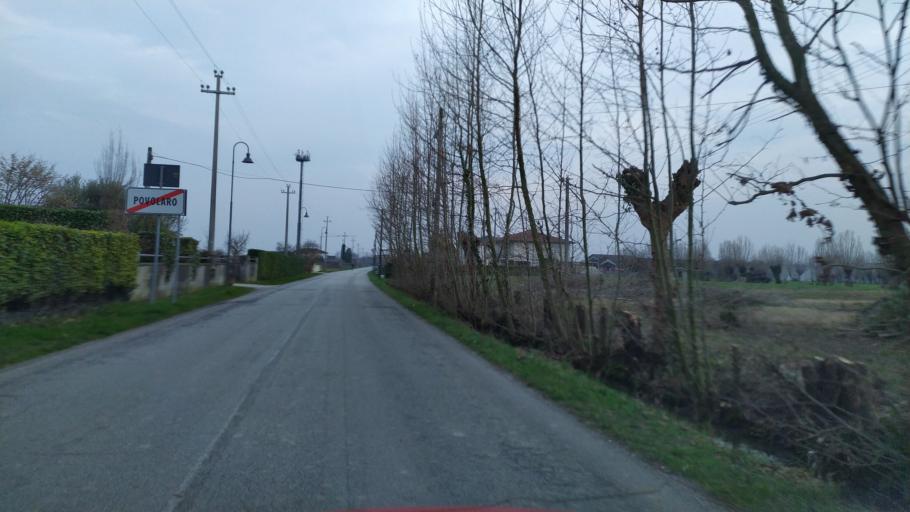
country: IT
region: Veneto
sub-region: Provincia di Vicenza
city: Vigardolo
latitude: 45.6237
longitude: 11.5779
